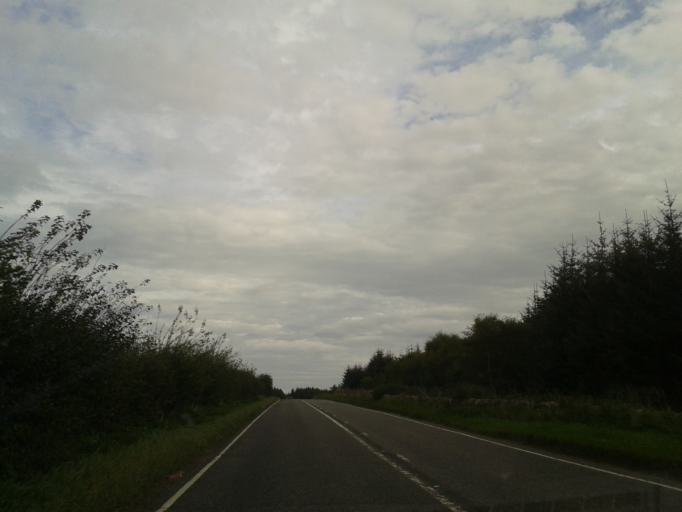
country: GB
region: Scotland
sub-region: Moray
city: Findochty
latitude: 57.6746
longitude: -2.9096
